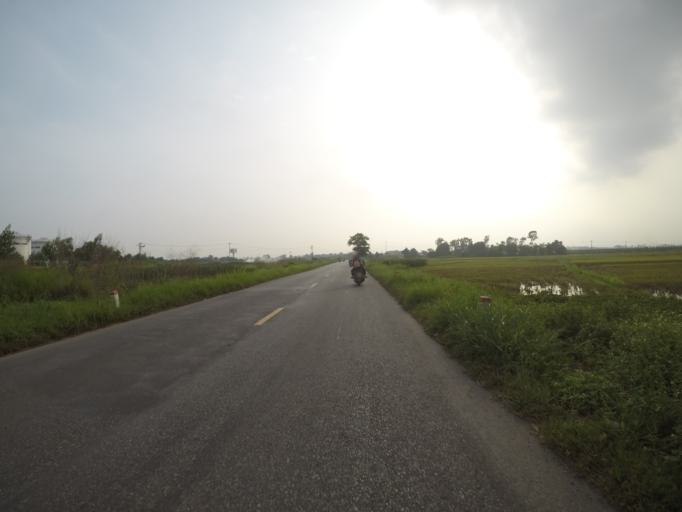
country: VN
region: Ha Noi
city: Me Linh
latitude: 21.2232
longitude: 105.7770
